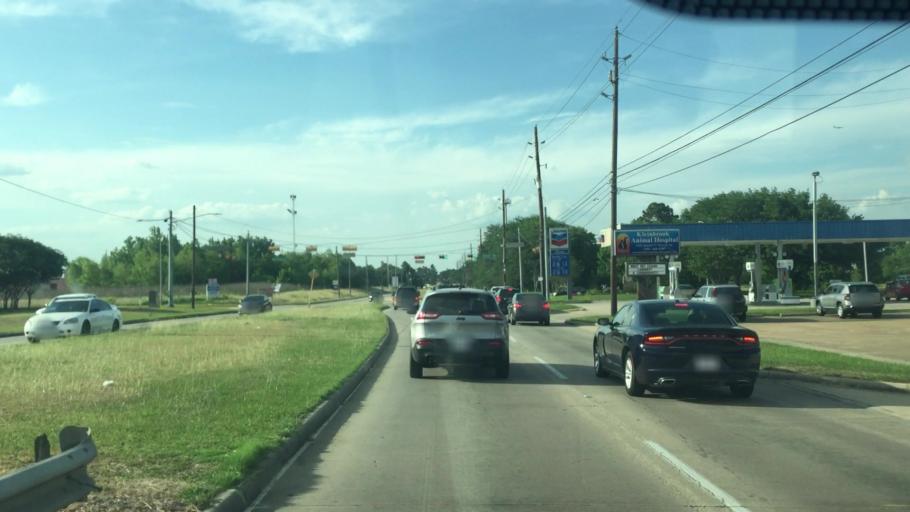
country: US
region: Texas
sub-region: Harris County
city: Hudson
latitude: 29.9559
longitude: -95.4984
